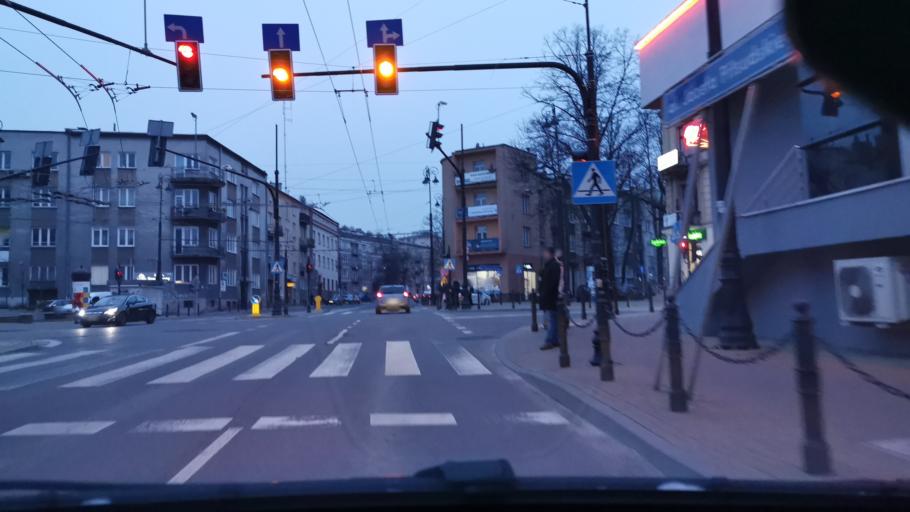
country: PL
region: Lublin Voivodeship
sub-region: Powiat lubelski
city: Lublin
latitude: 51.2415
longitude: 22.5552
